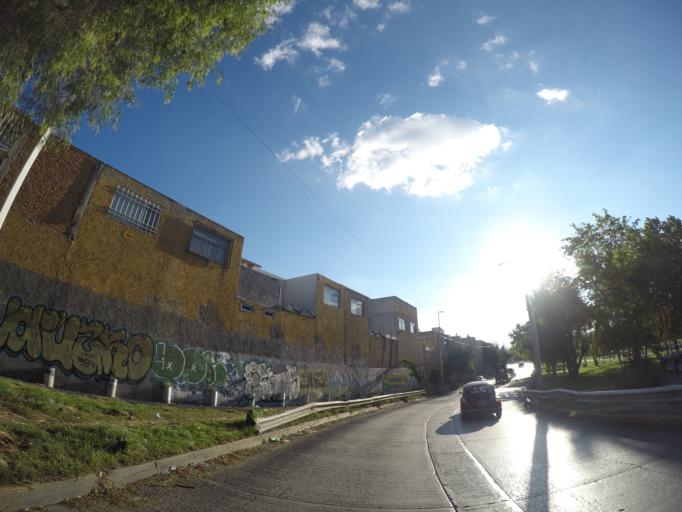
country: MX
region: San Luis Potosi
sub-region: San Luis Potosi
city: San Luis Potosi
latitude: 22.1578
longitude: -101.0003
